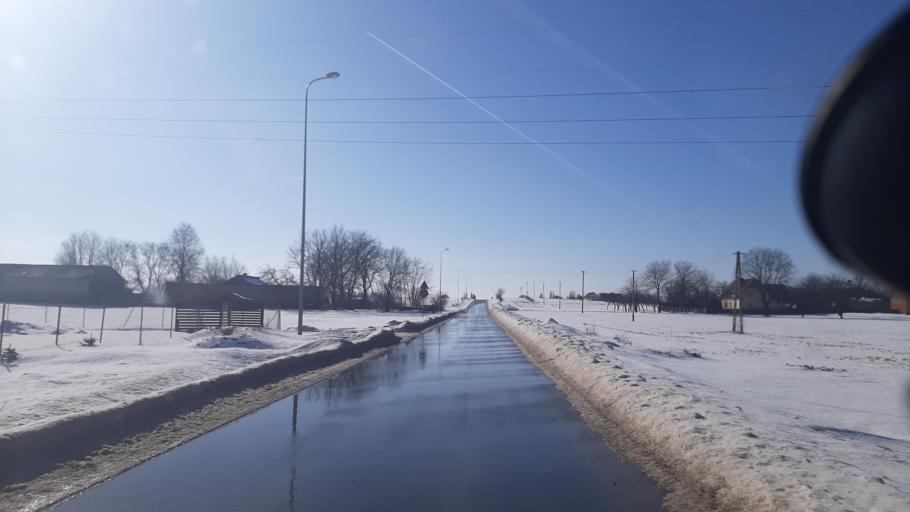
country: PL
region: Lublin Voivodeship
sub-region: Powiat lubelski
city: Garbow
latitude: 51.3353
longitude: 22.3353
